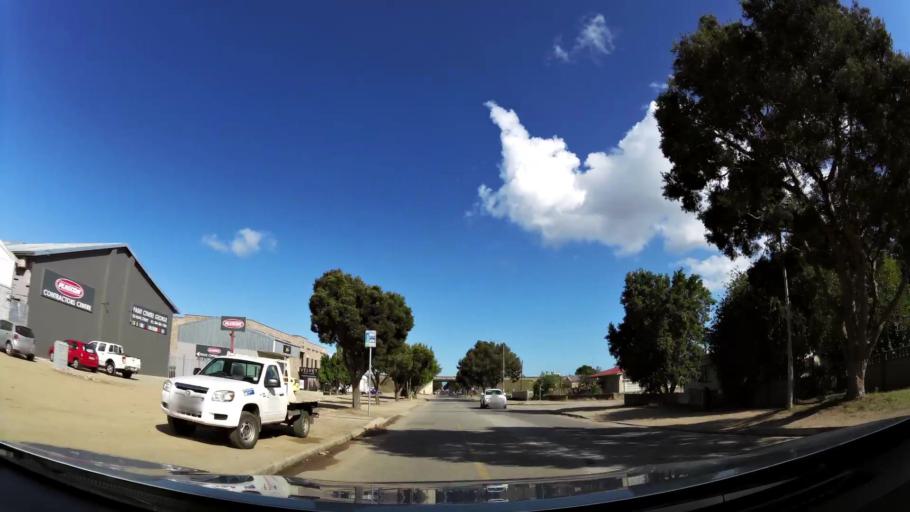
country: ZA
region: Western Cape
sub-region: Eden District Municipality
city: George
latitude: -33.9681
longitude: 22.4646
